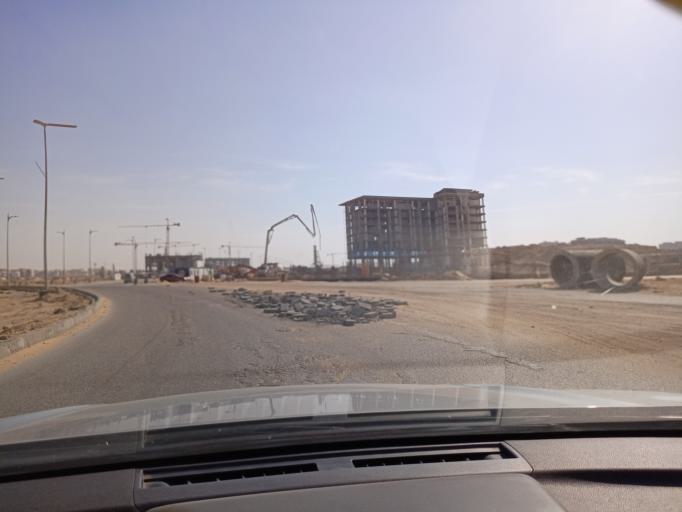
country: EG
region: Muhafazat al Qalyubiyah
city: Al Khankah
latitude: 30.0384
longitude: 31.6830
